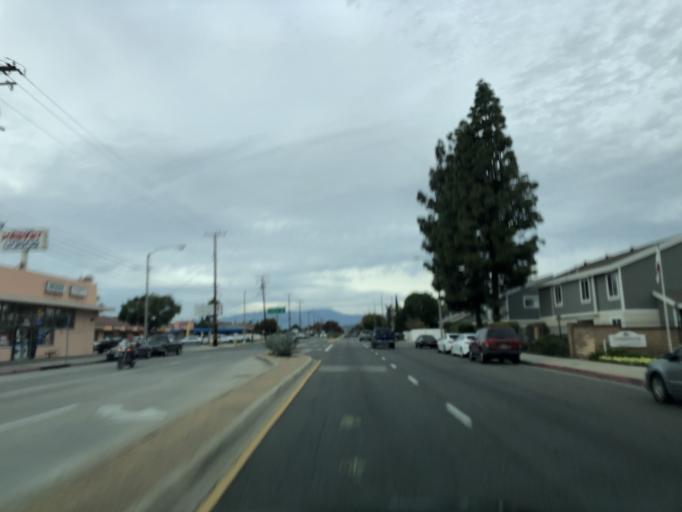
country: US
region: California
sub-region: Los Angeles County
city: South Whittier
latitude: 33.9260
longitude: -118.0464
